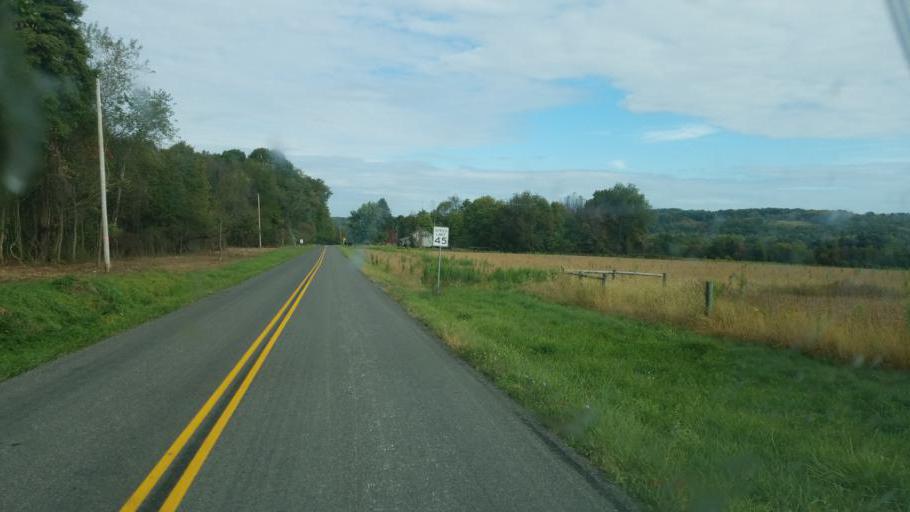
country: US
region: Pennsylvania
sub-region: Mercer County
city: Mercer
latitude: 41.3319
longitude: -80.2609
